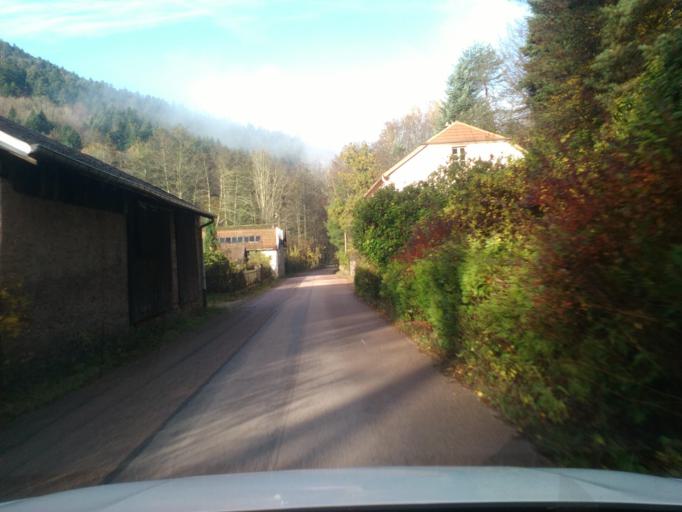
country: FR
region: Lorraine
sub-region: Departement des Vosges
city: Senones
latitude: 48.4209
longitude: 7.0410
